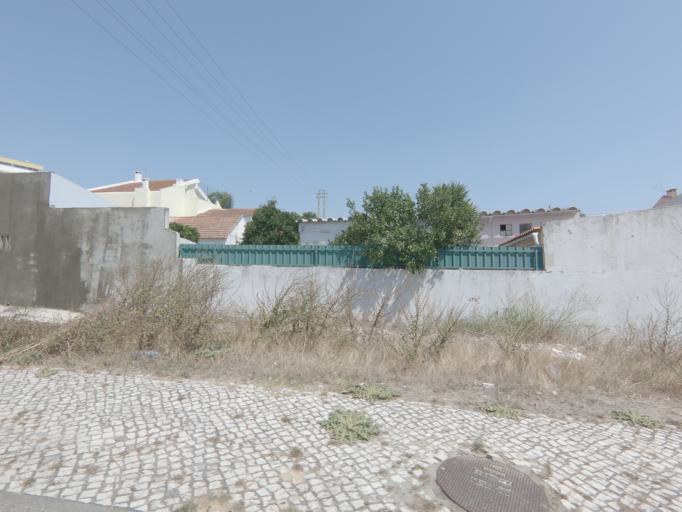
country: PT
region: Setubal
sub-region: Setubal
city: Setubal
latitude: 38.5441
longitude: -8.8832
